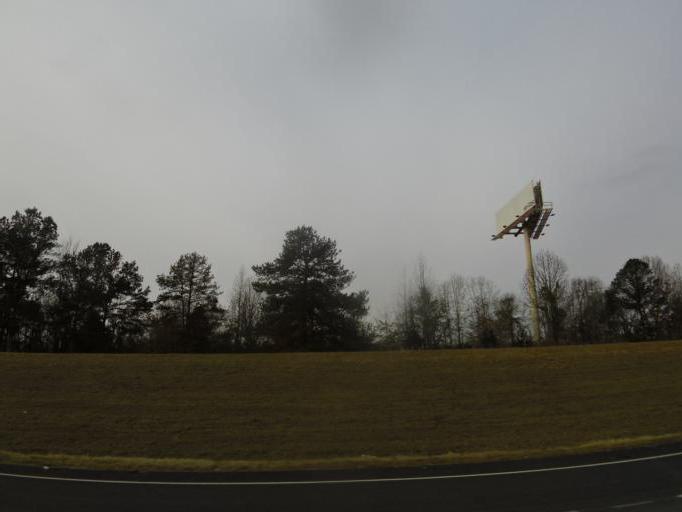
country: US
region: Alabama
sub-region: Elmore County
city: Millbrook
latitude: 32.4549
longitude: -86.3847
